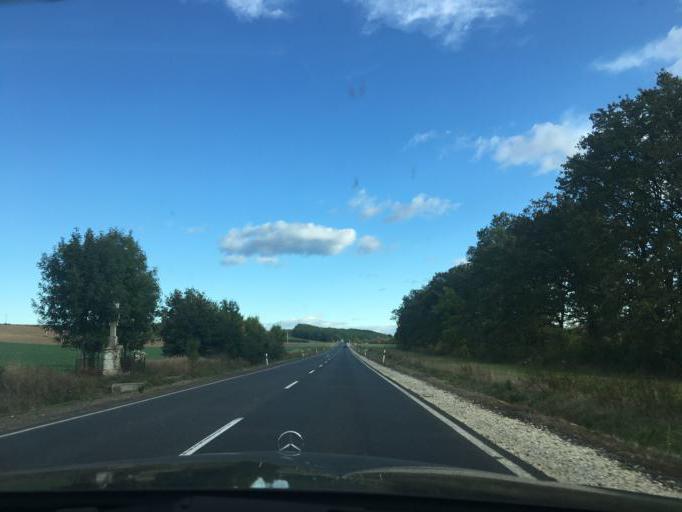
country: HU
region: Borsod-Abauj-Zemplen
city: Encs
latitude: 48.3666
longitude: 21.1408
